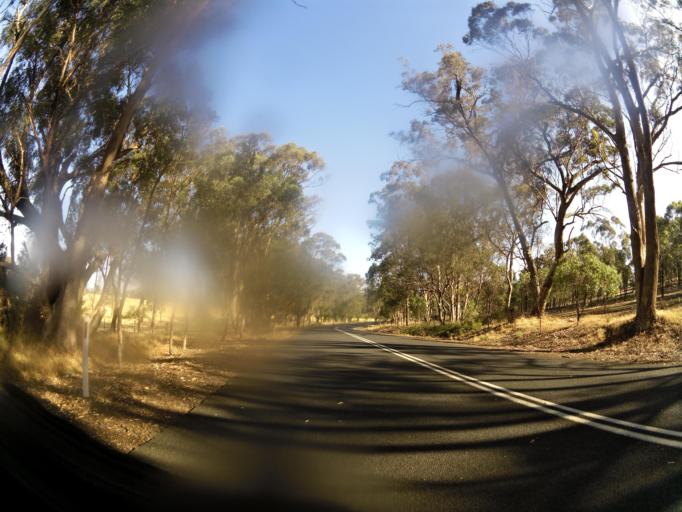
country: AU
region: Victoria
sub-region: Murrindindi
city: Kinglake West
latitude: -37.0066
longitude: 145.1234
